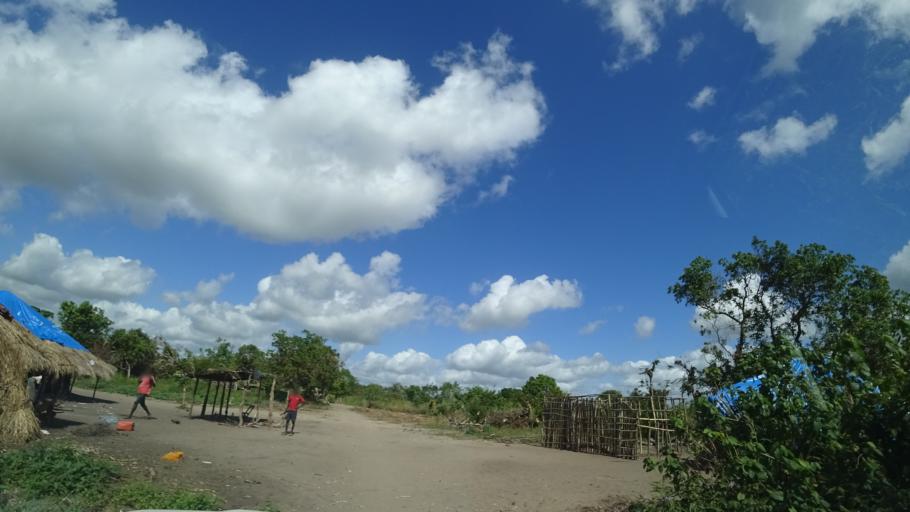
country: MZ
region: Sofala
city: Dondo
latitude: -19.3577
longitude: 34.5791
